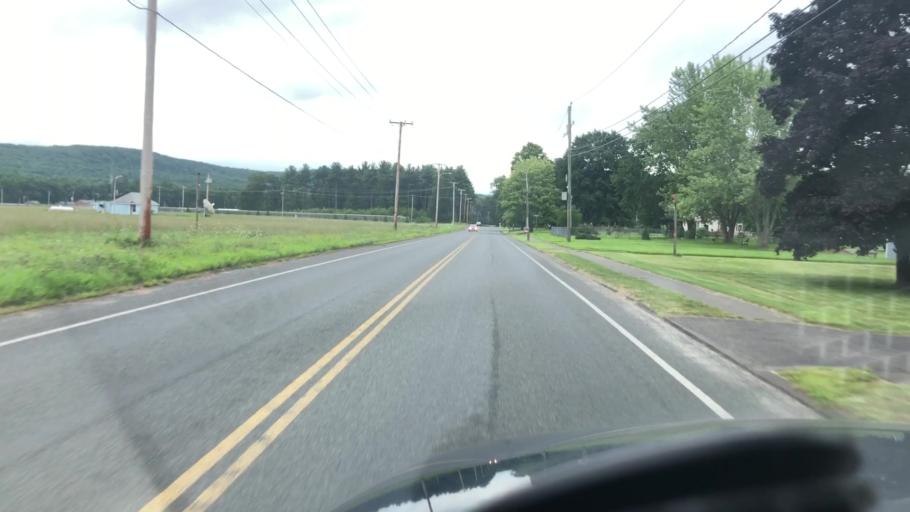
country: US
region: Massachusetts
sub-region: Hampshire County
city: Southampton
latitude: 42.1948
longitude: -72.6873
